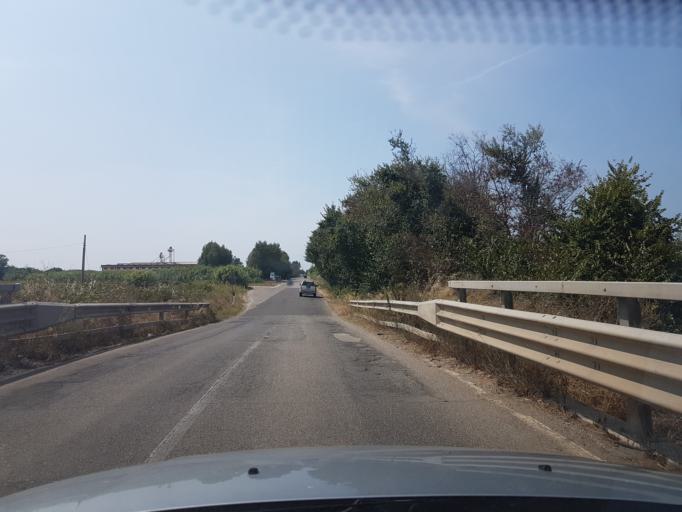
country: IT
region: Sardinia
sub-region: Provincia di Oristano
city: Solanas
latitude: 39.9203
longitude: 8.5481
